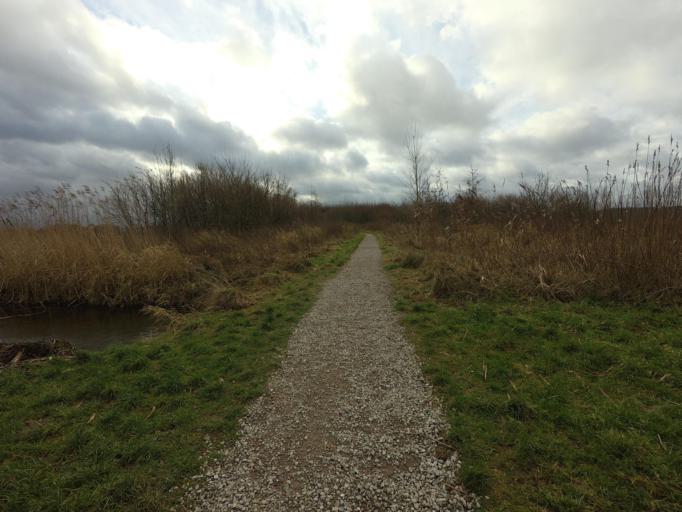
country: NL
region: Utrecht
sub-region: Stichtse Vecht
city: Spechtenkamp
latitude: 52.1136
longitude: 5.0037
